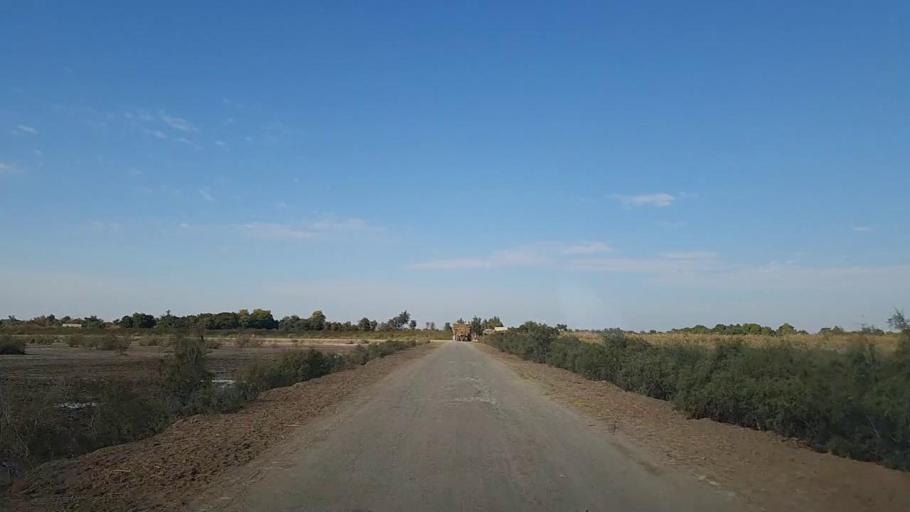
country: PK
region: Sindh
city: Khadro
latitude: 26.3006
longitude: 68.8202
